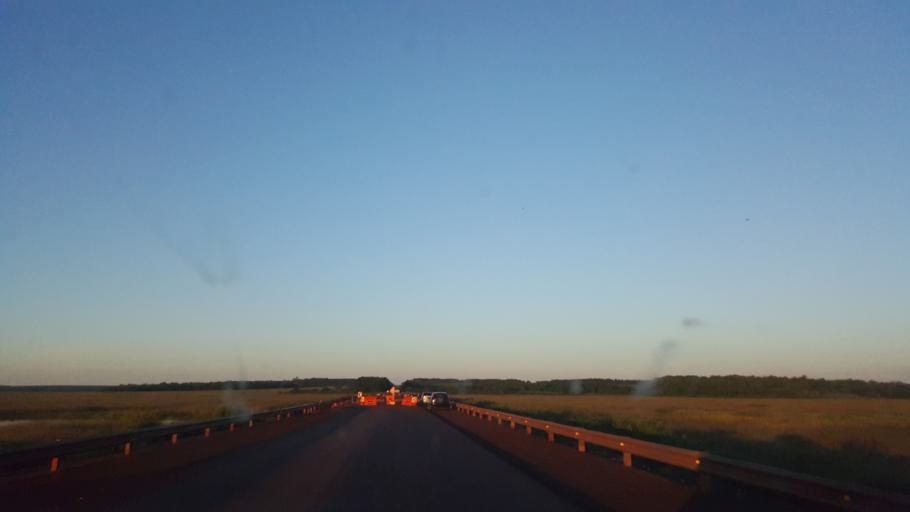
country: AR
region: Corrientes
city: Santo Tome
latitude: -28.3838
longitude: -55.9624
